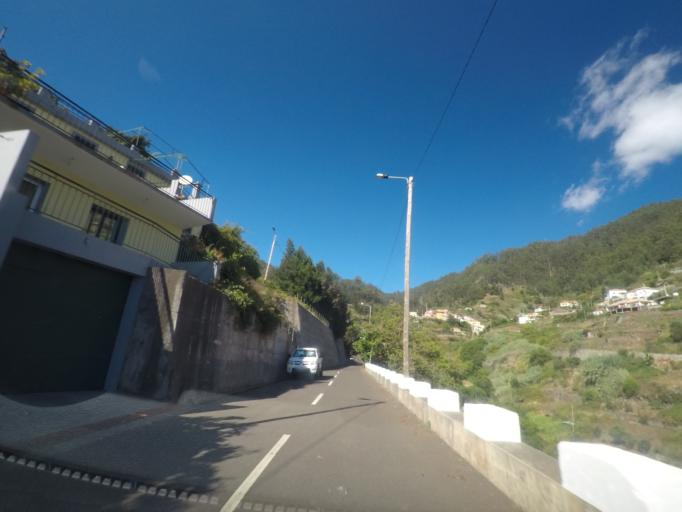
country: PT
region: Madeira
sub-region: Ribeira Brava
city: Campanario
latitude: 32.6775
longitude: -17.0230
